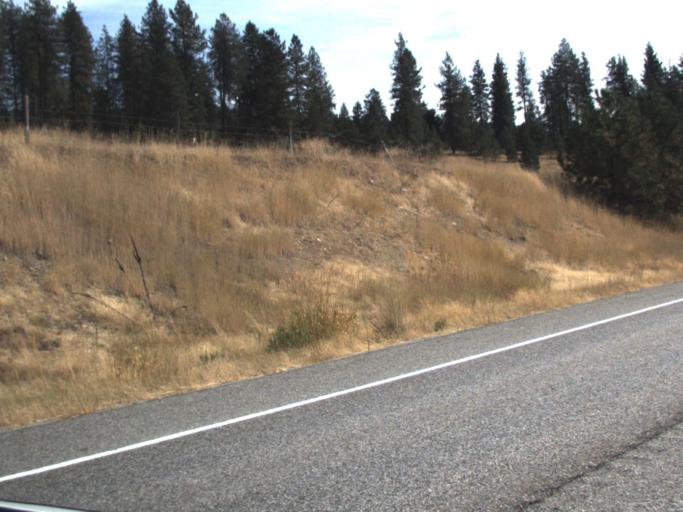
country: US
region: Washington
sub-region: Stevens County
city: Chewelah
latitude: 48.1665
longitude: -117.6996
